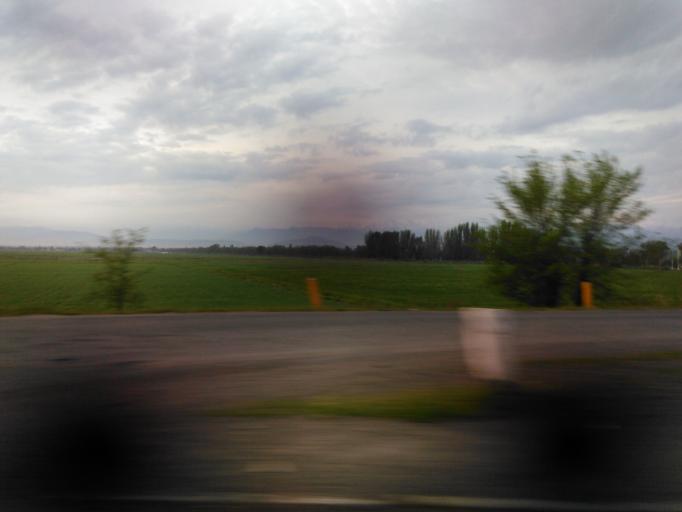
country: KG
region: Chuy
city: Bishkek
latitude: 42.9346
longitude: 74.4977
